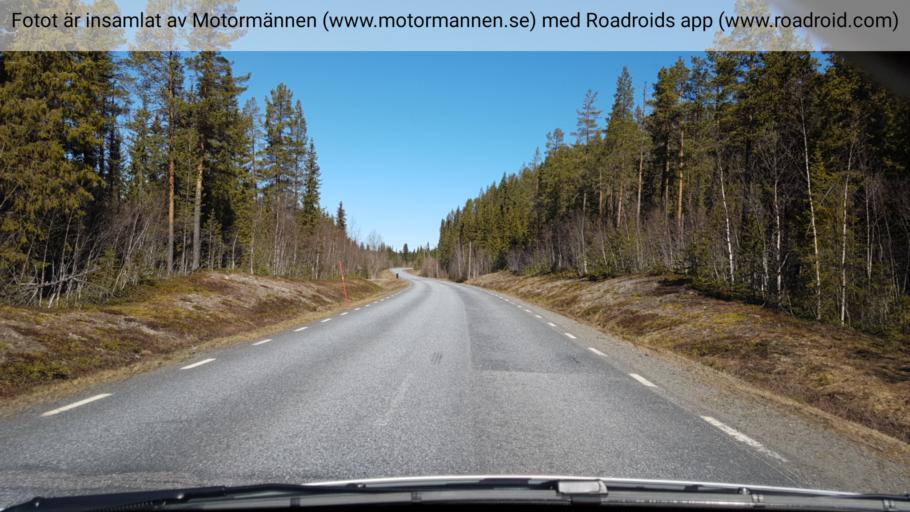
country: SE
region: Vaesterbotten
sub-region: Vilhelmina Kommun
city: Sjoberg
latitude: 64.9510
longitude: 15.8624
